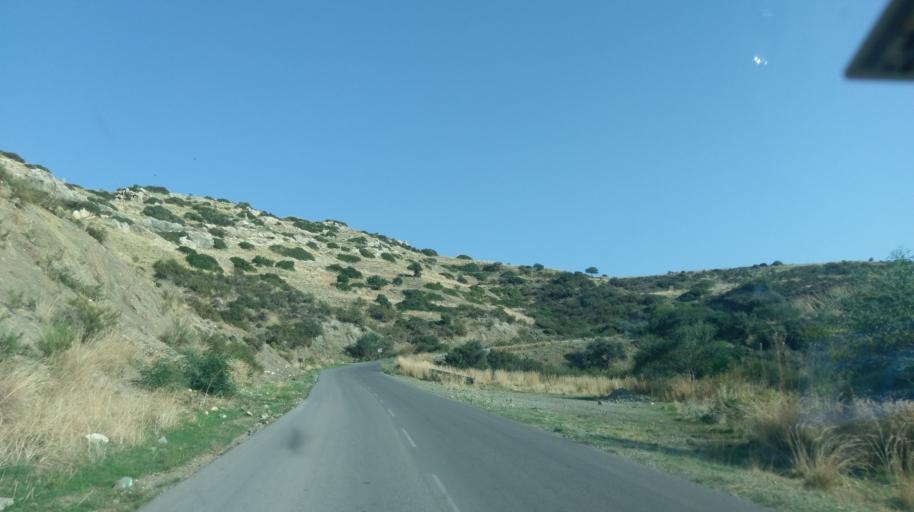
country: CY
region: Lefkosia
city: Kato Pyrgos
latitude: 35.1652
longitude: 32.7514
